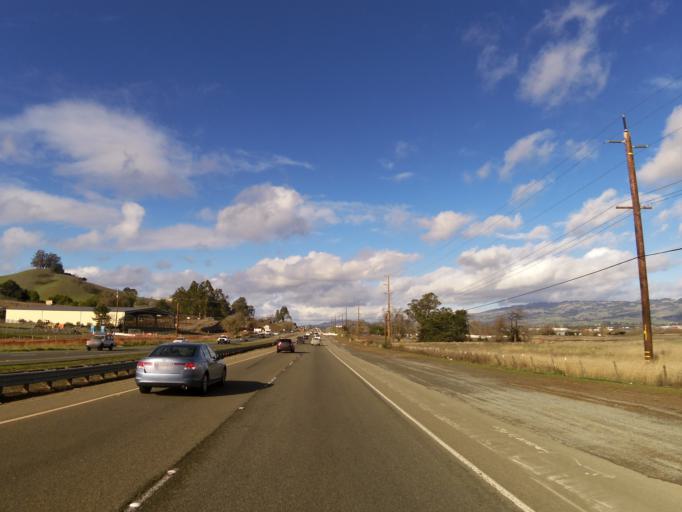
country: US
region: California
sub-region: Sonoma County
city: Petaluma
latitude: 38.2077
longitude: -122.5993
